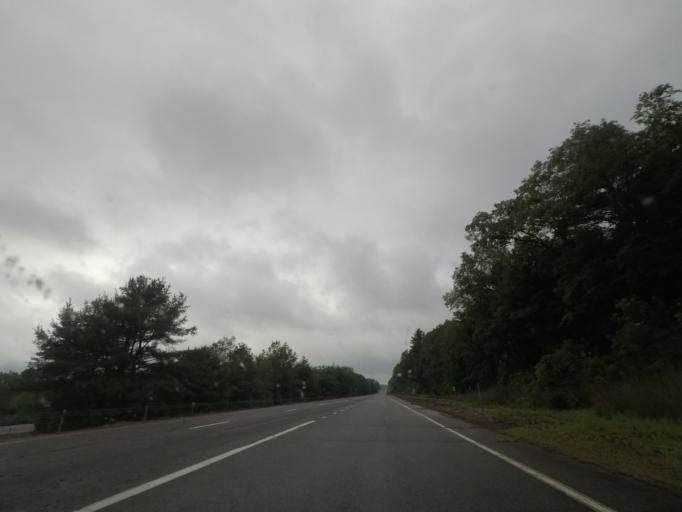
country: US
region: Massachusetts
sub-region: Worcester County
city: Webster
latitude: 42.0111
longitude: -71.8555
